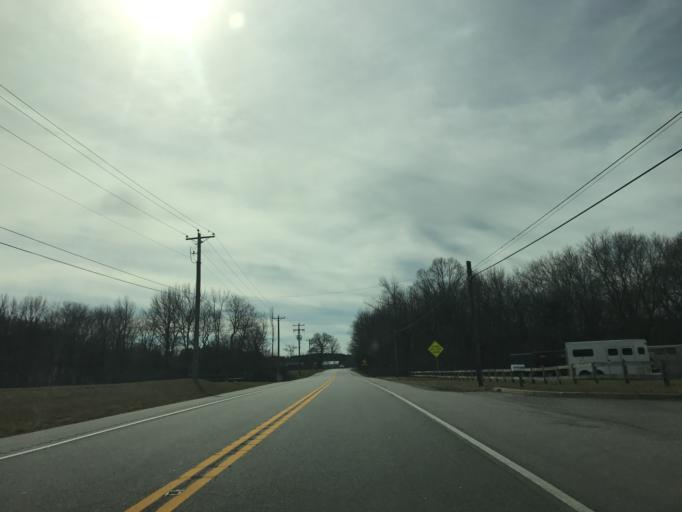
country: US
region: Maryland
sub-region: Queen Anne's County
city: Kingstown
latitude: 39.1205
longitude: -76.0150
